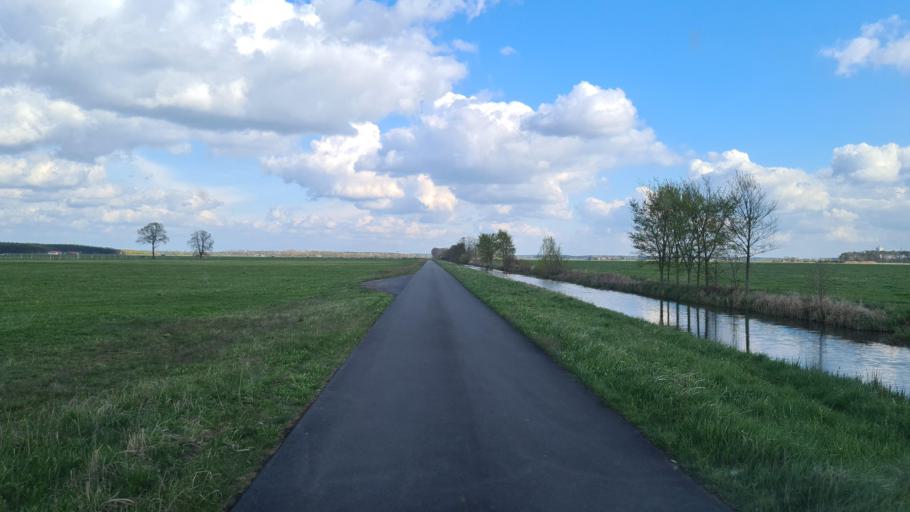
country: DE
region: Brandenburg
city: Herzberg
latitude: 51.7293
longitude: 13.2425
